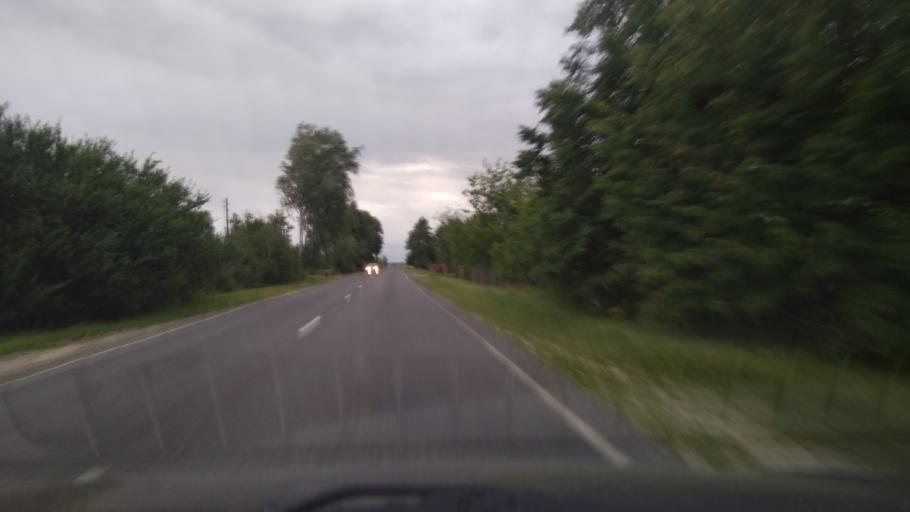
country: BY
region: Brest
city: Byaroza
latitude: 52.4249
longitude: 24.9811
